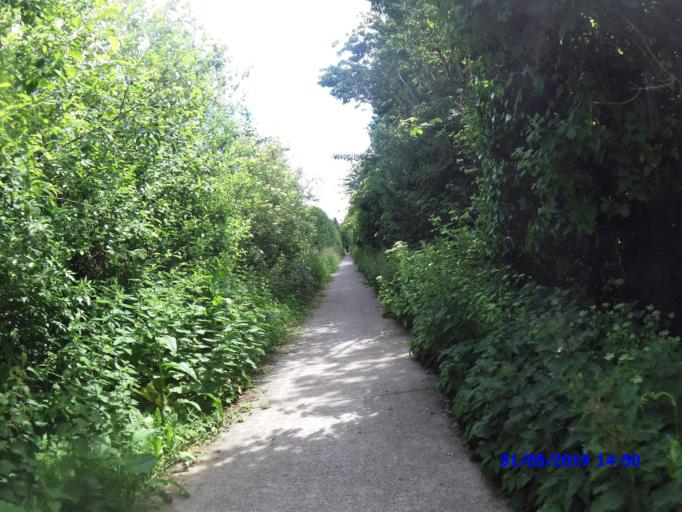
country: FR
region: Nord-Pas-de-Calais
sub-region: Departement du Nord
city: Comines
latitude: 50.7879
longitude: 2.9648
